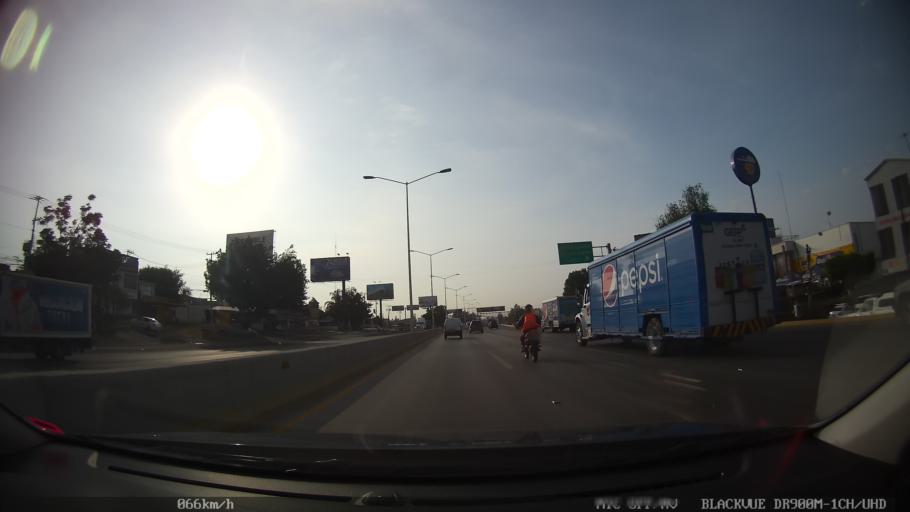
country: MX
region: Jalisco
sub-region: Zapopan
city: Zapopan
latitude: 20.7321
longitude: -103.3553
